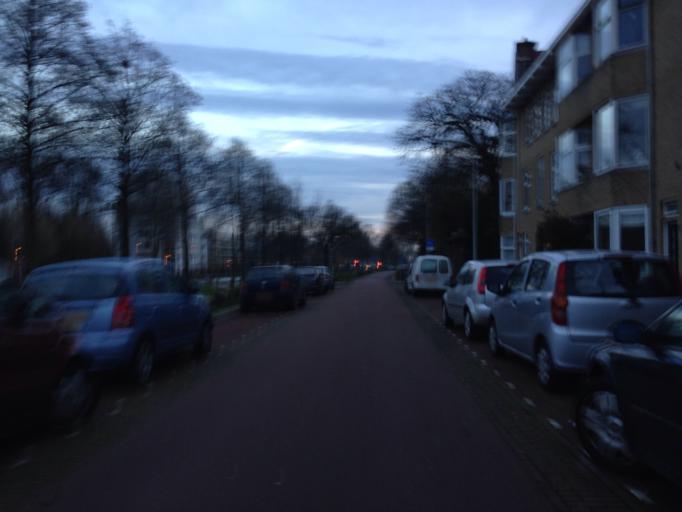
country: NL
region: South Holland
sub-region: Gemeente Leidschendam-Voorburg
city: Voorburg
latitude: 52.0617
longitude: 4.3403
